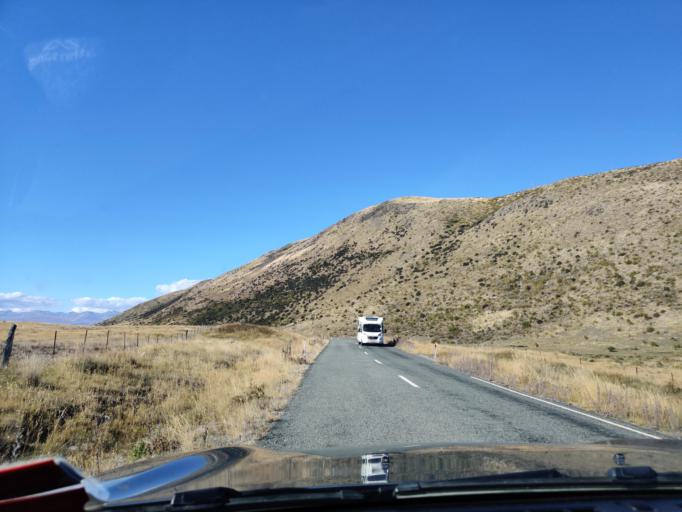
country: NZ
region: Canterbury
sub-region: Timaru District
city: Pleasant Point
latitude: -43.9889
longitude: 170.4522
